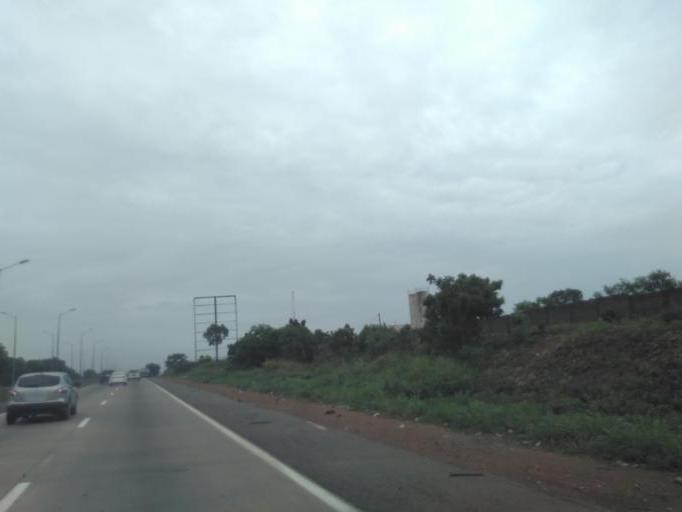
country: GH
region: Greater Accra
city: Medina Estates
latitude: 5.6366
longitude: -0.1388
